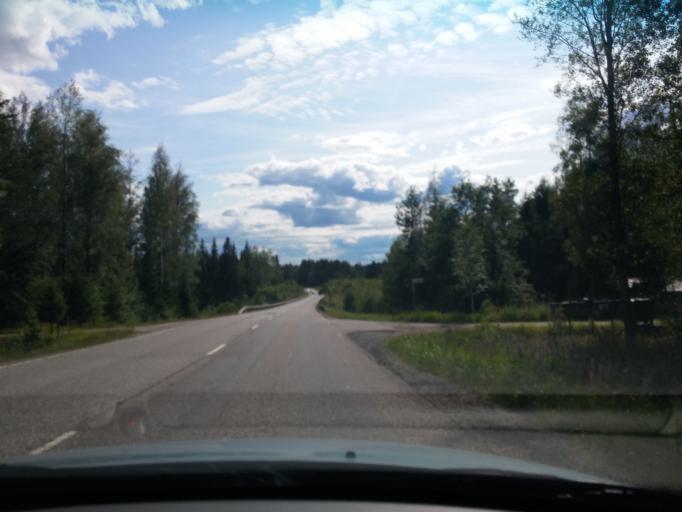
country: FI
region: Central Finland
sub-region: Keuruu
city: Keuruu
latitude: 62.2828
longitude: 24.6944
